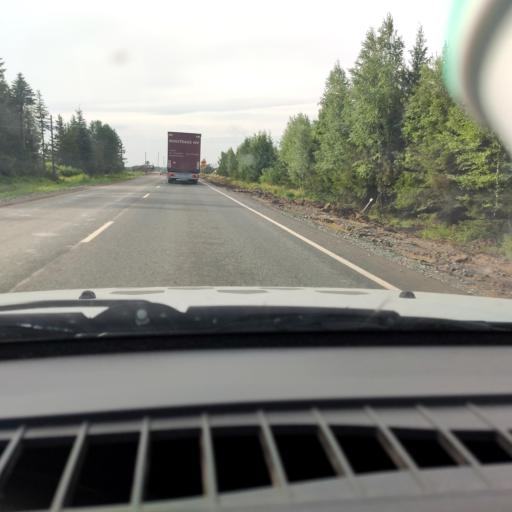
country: RU
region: Kirov
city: Kostino
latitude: 58.8344
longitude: 53.3055
